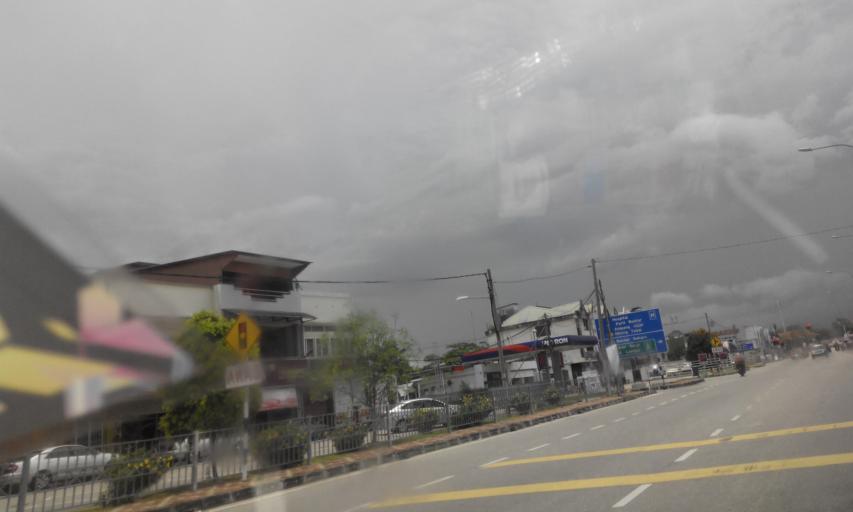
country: MY
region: Perak
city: Parit Buntar
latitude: 5.1260
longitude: 100.4889
